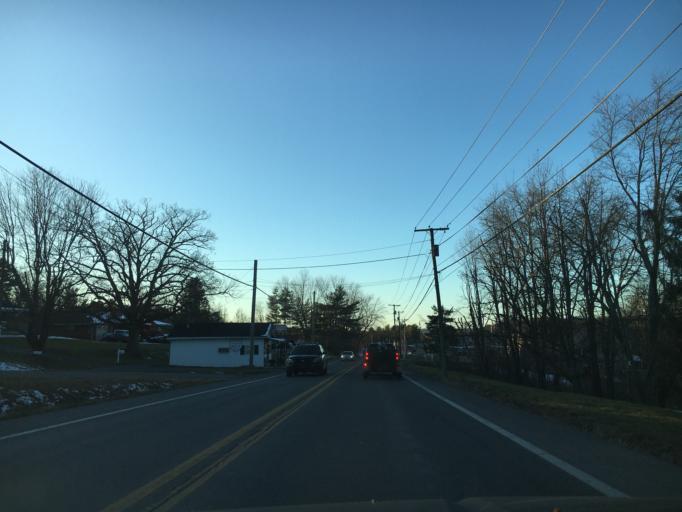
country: US
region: West Virginia
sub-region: Raleigh County
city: Daniels
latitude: 37.7419
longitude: -81.1198
